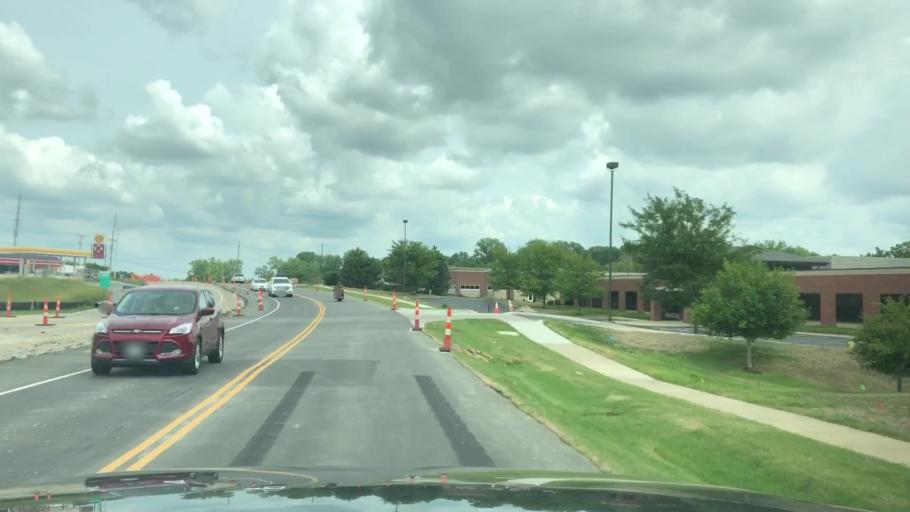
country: US
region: Missouri
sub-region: Saint Charles County
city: Saint Peters
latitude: 38.8028
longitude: -90.5551
